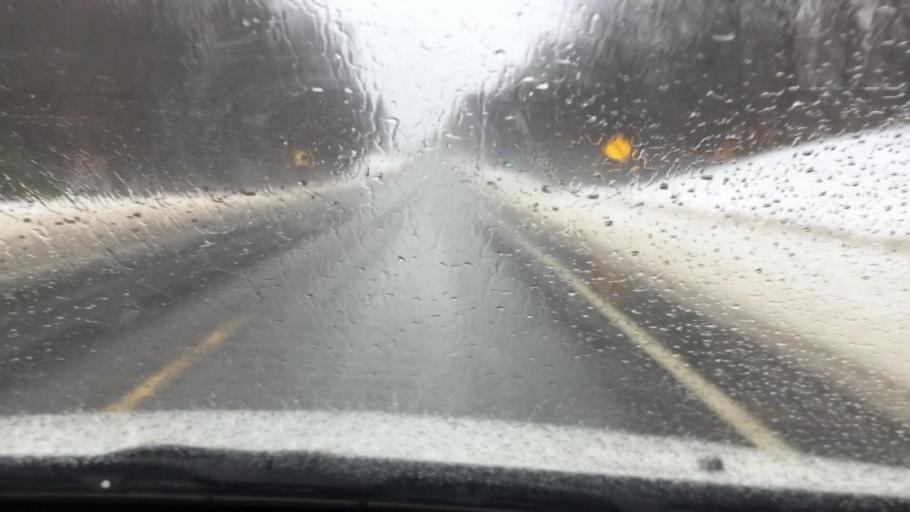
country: US
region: Michigan
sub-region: Antrim County
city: Mancelona
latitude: 44.9771
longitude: -85.0544
